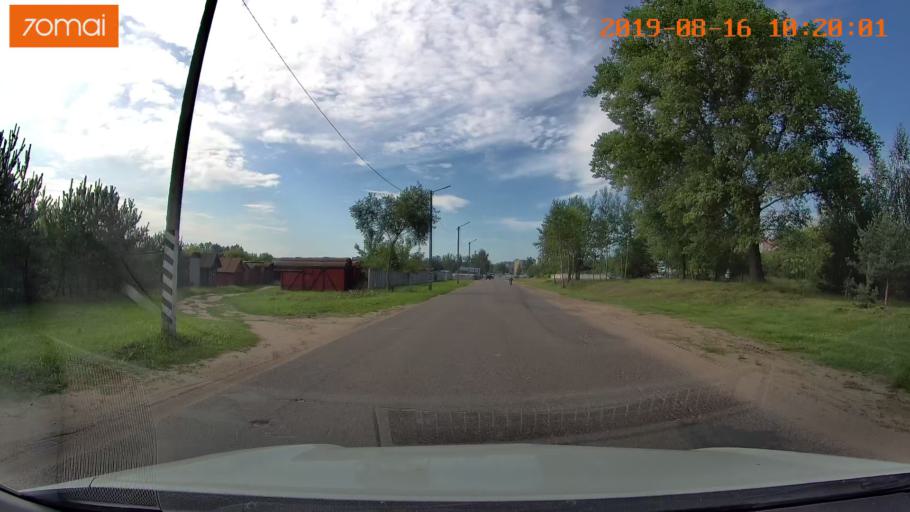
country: BY
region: Mogilev
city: Asipovichy
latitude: 53.3040
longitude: 28.6638
